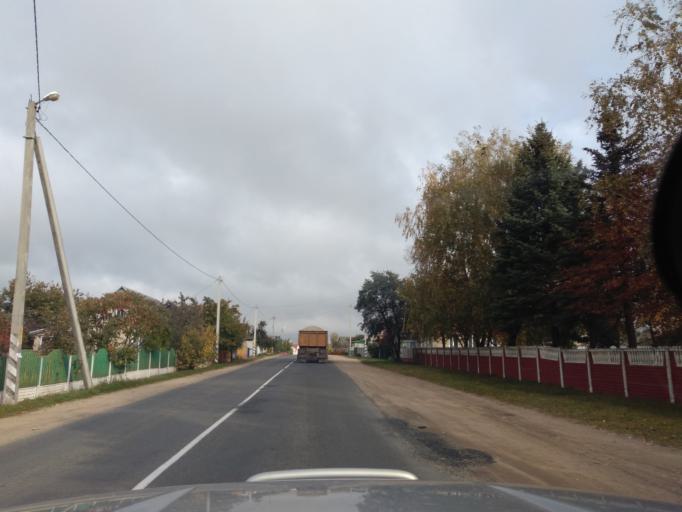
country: BY
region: Minsk
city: Kapyl'
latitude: 53.1499
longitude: 27.0747
